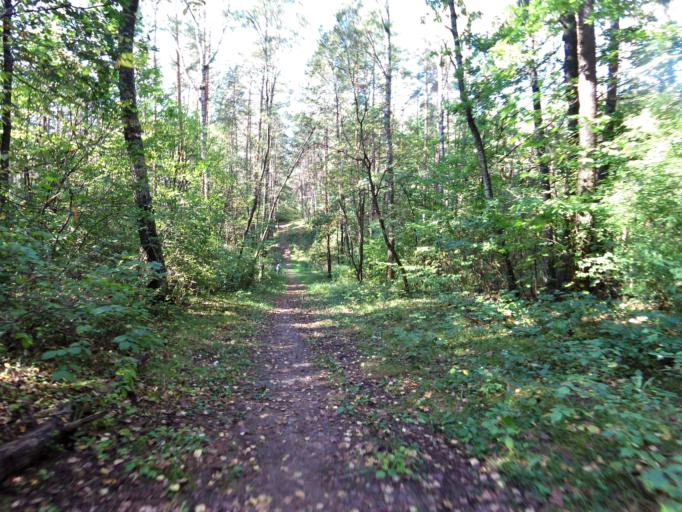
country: LT
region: Vilnius County
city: Pilaite
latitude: 54.6925
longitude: 25.1989
